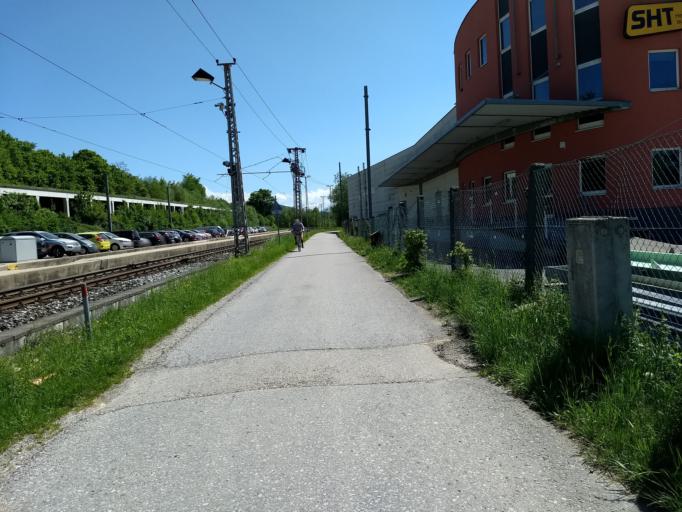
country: AT
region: Salzburg
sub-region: Politischer Bezirk Salzburg-Umgebung
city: Bergheim
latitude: 47.8395
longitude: 13.0207
